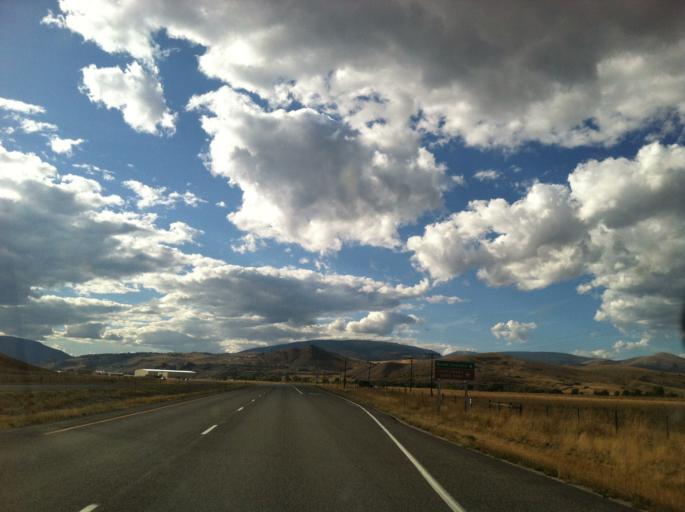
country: US
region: Montana
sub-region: Deer Lodge County
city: Anaconda
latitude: 46.1268
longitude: -112.8933
